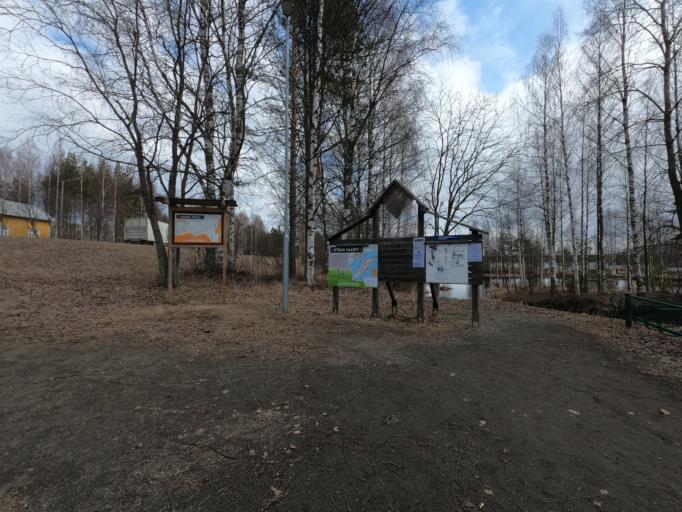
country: FI
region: North Karelia
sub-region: Joensuu
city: Joensuu
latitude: 62.6198
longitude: 29.8679
